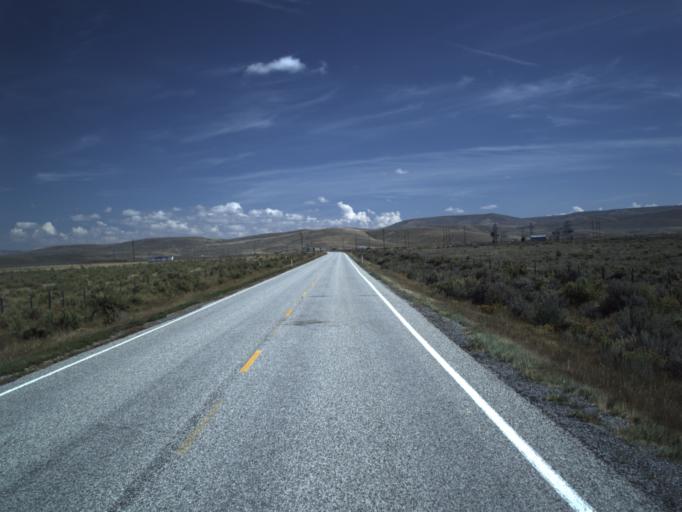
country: US
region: Utah
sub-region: Rich County
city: Randolph
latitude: 41.7789
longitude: -111.0540
